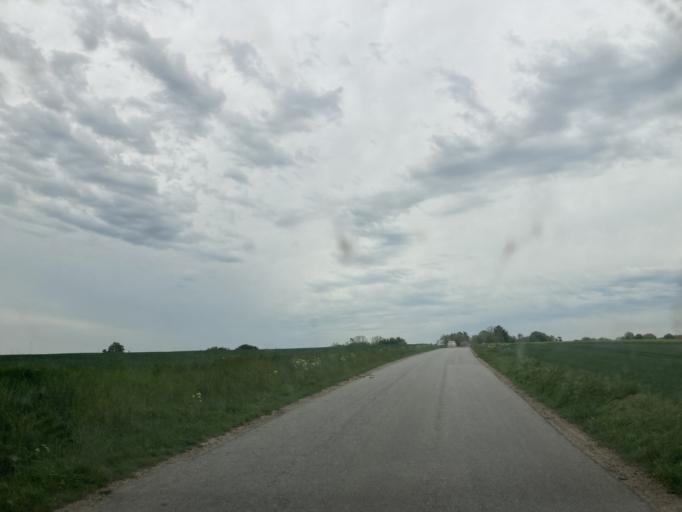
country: DK
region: Zealand
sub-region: Roskilde Kommune
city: Svogerslev
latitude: 55.6697
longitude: 12.0029
